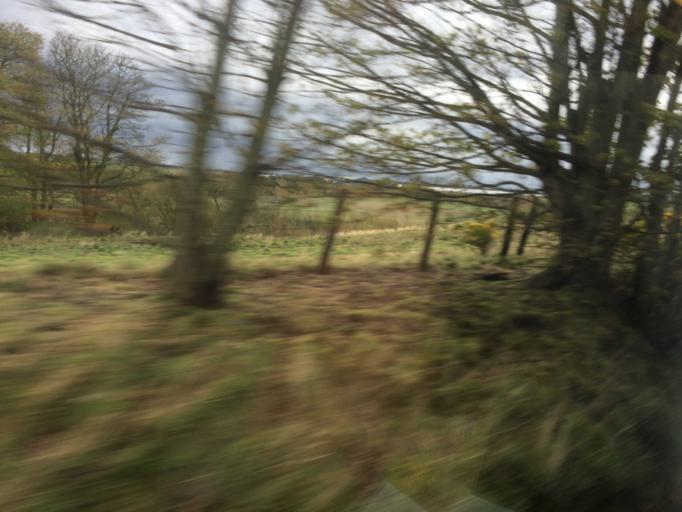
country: GB
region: Scotland
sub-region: Angus
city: Montrose
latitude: 56.6482
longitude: -2.5344
